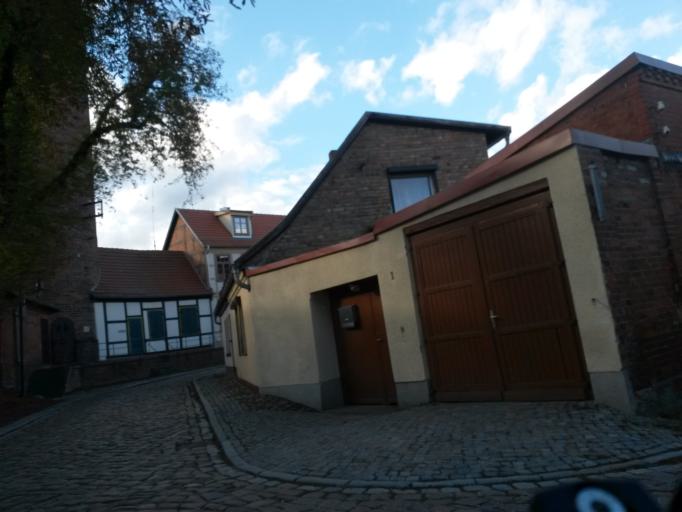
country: DE
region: Saxony-Anhalt
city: Tangermunde
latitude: 52.5406
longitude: 11.9678
